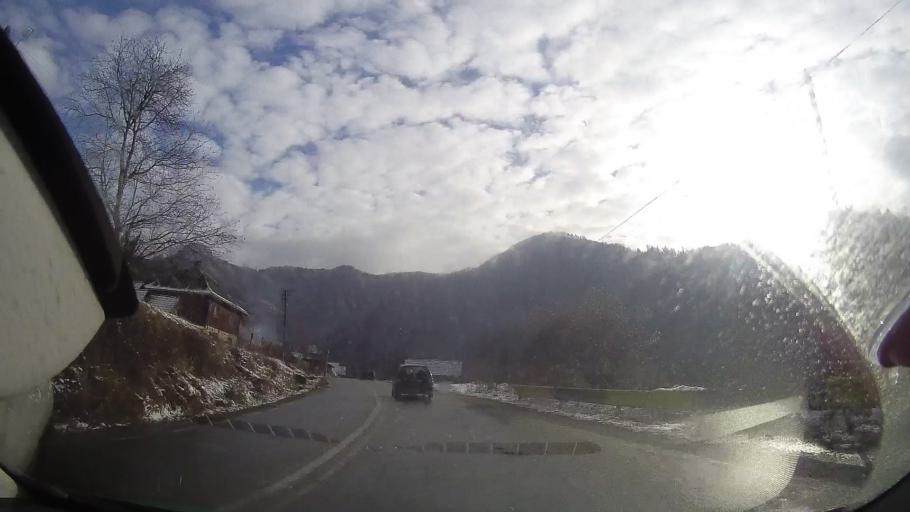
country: RO
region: Alba
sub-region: Oras Baia de Aries
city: Baia de Aries
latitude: 46.3906
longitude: 23.2909
